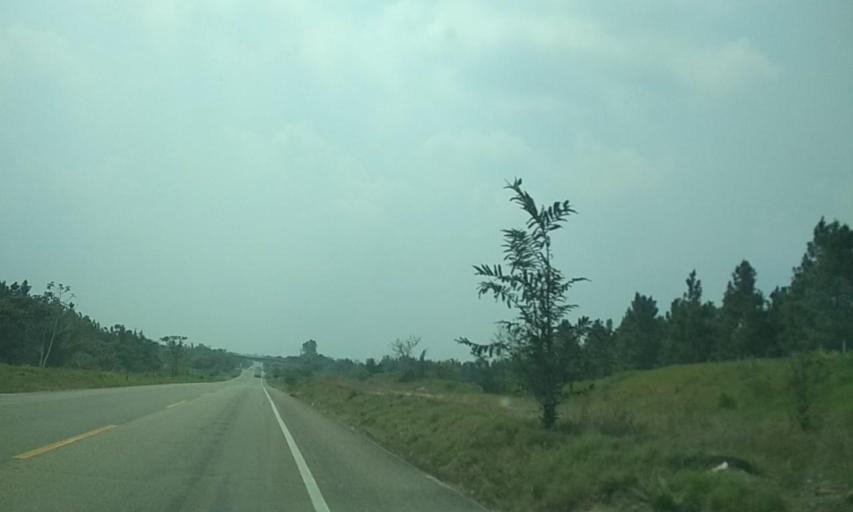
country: MX
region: Tabasco
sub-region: Huimanguillo
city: Francisco Rueda
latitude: 17.7544
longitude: -94.0003
